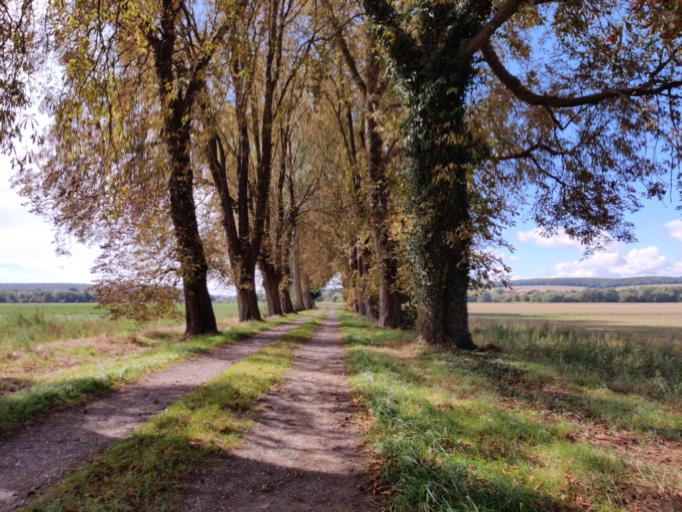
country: DE
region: Lower Saxony
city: Sehlde
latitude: 52.0462
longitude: 10.2809
